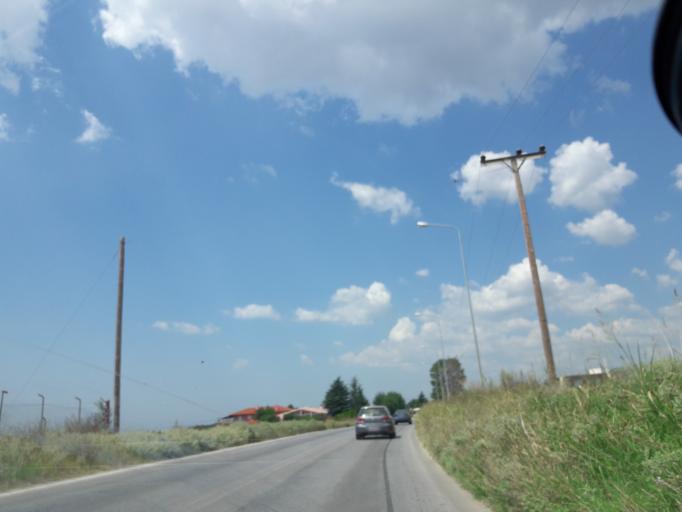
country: GR
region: Central Macedonia
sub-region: Nomos Thessalonikis
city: Souroti
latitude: 40.5024
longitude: 23.0954
